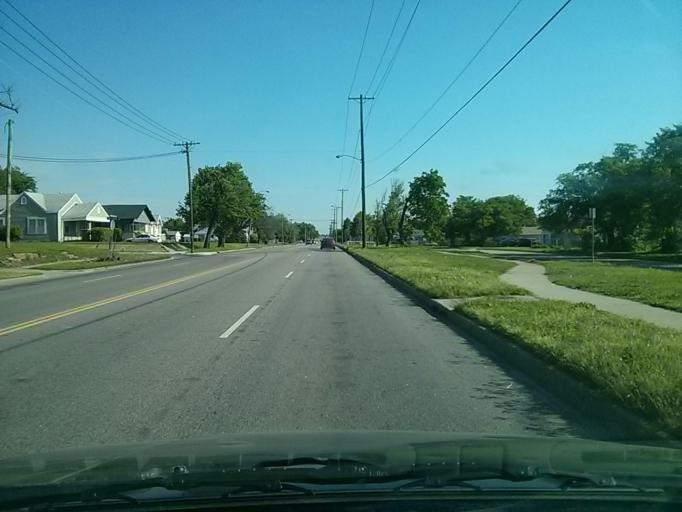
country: US
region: Oklahoma
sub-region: Tulsa County
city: Tulsa
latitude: 36.1851
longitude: -95.9934
